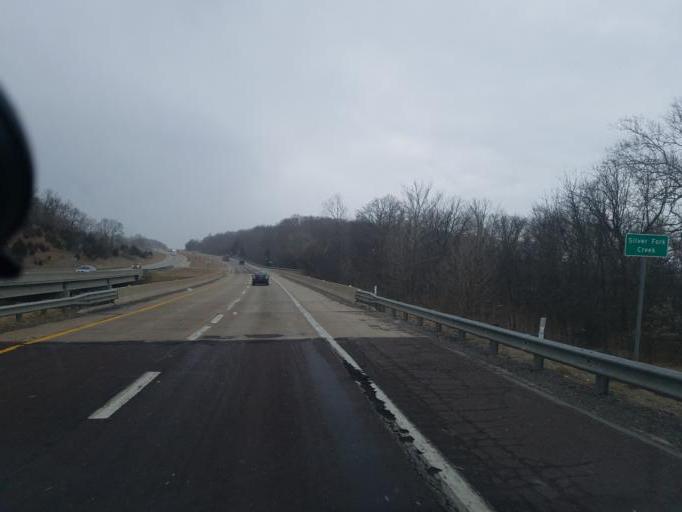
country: US
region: Missouri
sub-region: Boone County
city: Hallsville
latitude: 39.1256
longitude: -92.3331
